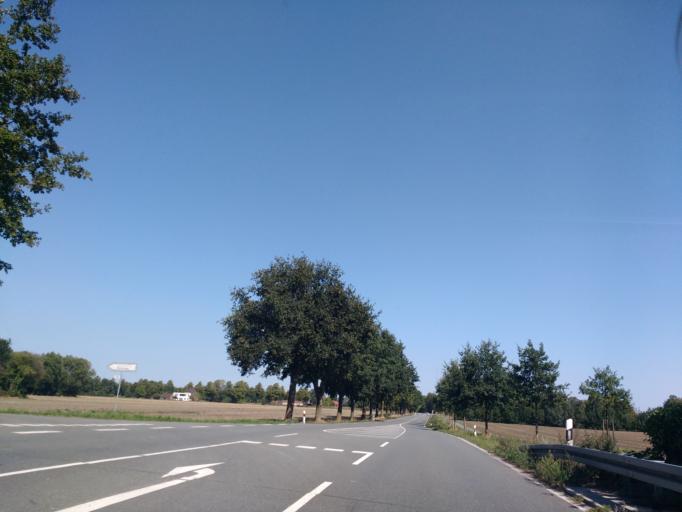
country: DE
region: North Rhine-Westphalia
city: Rietberg
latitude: 51.8121
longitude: 8.4110
